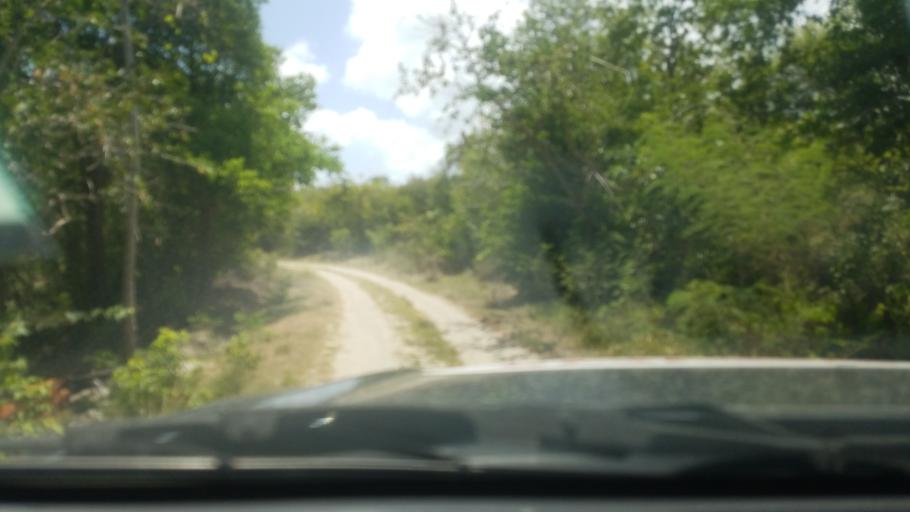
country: LC
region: Vieux-Fort
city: Vieux Fort
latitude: 13.7521
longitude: -60.9395
